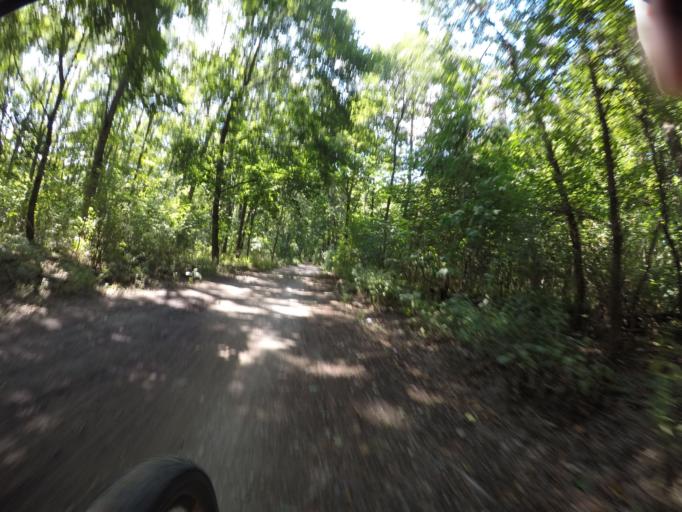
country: AT
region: Lower Austria
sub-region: Politischer Bezirk Ganserndorf
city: Gross-Enzersdorf
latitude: 48.1825
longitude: 16.5016
